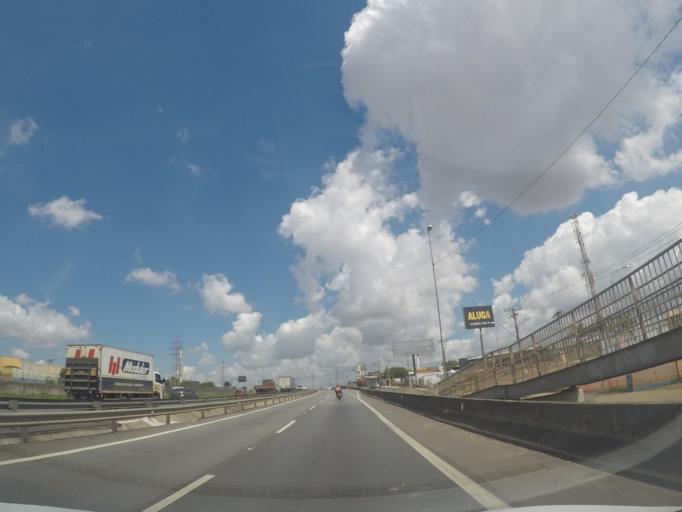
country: BR
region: Sao Paulo
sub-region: Hortolandia
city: Hortolandia
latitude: -22.8303
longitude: -47.1793
